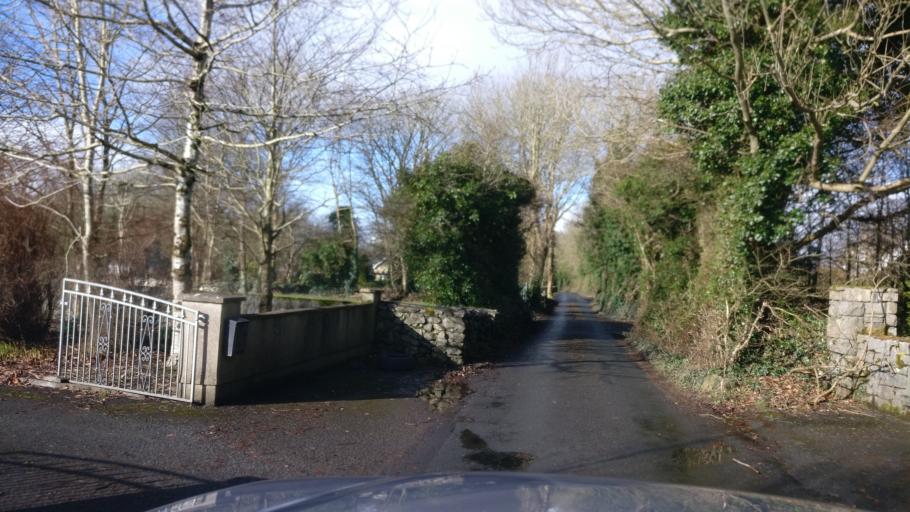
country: IE
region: Connaught
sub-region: County Galway
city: Athenry
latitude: 53.2285
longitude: -8.7449
